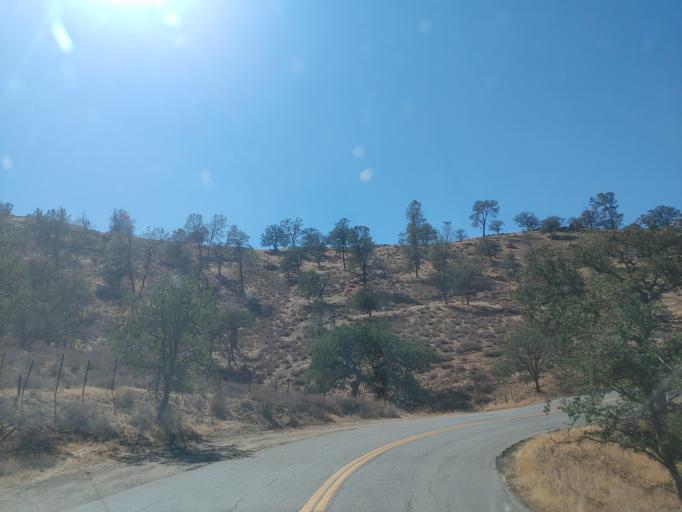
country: US
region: California
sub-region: Kern County
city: Golden Hills
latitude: 35.1939
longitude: -118.5312
